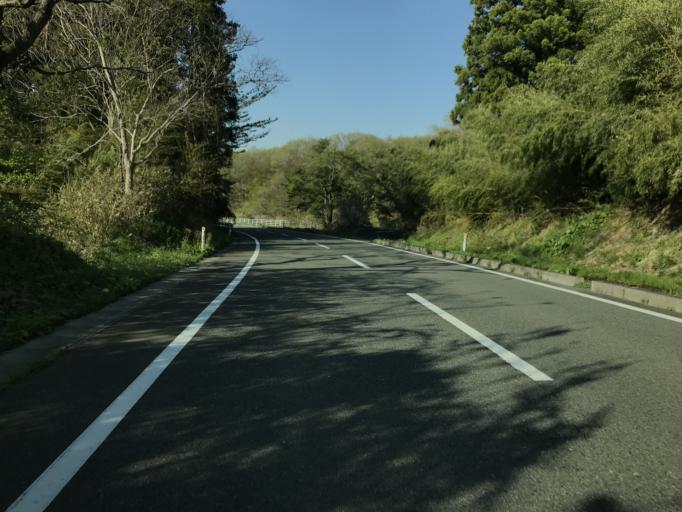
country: JP
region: Fukushima
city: Funehikimachi-funehiki
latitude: 37.5554
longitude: 140.7391
